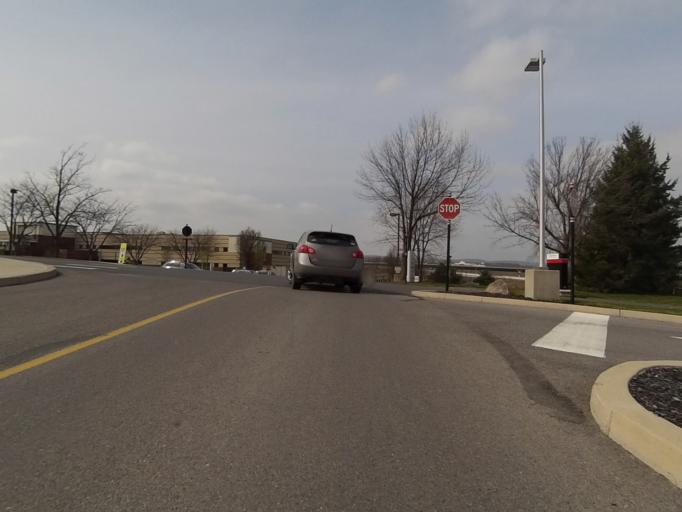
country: US
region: Pennsylvania
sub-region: Centre County
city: Houserville
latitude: 40.8198
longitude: -77.8438
